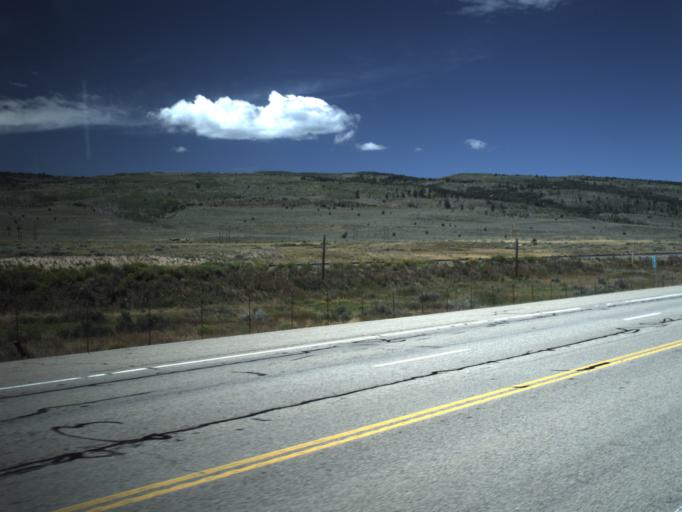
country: US
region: Utah
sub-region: Carbon County
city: Helper
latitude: 39.8762
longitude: -111.0372
